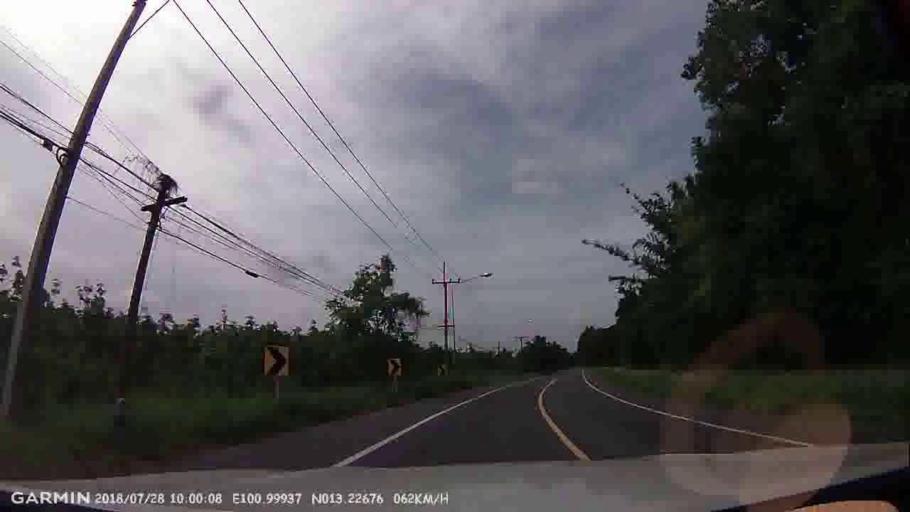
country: TH
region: Chon Buri
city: Si Racha
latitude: 13.2265
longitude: 100.9995
